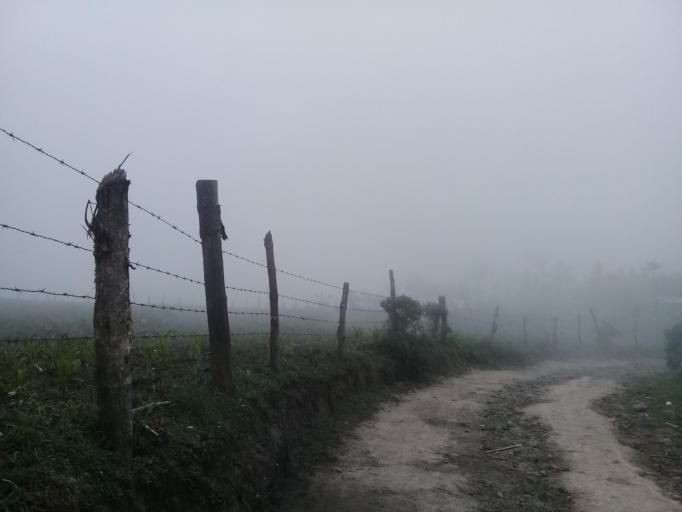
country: MX
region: Veracruz
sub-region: Mariano Escobedo
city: Texmola
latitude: 18.9598
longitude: -97.2179
